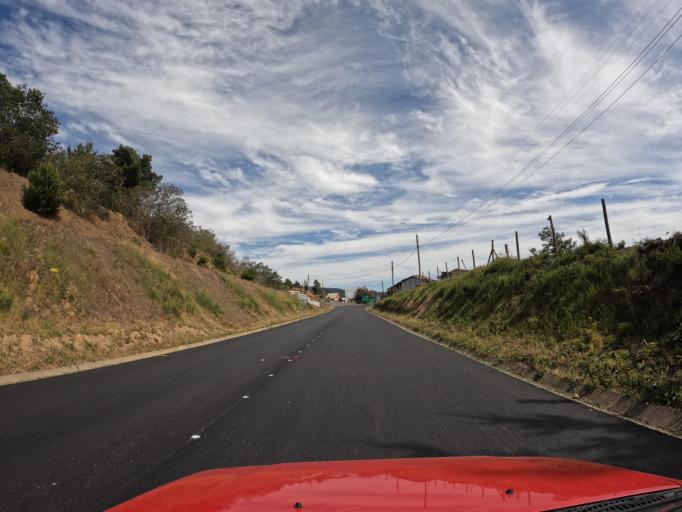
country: CL
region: Maule
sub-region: Provincia de Talca
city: Constitucion
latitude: -35.0839
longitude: -72.0172
